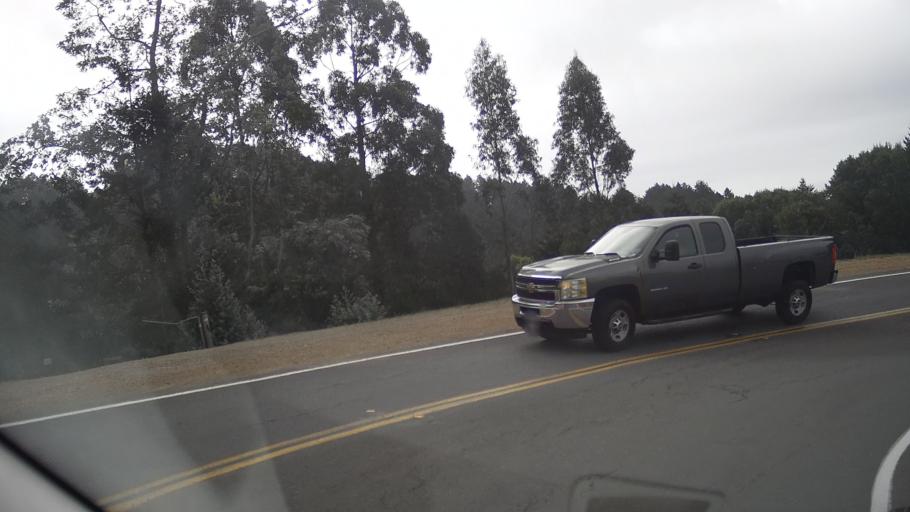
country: US
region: California
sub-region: Marin County
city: Bolinas
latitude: 37.8920
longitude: -122.6228
